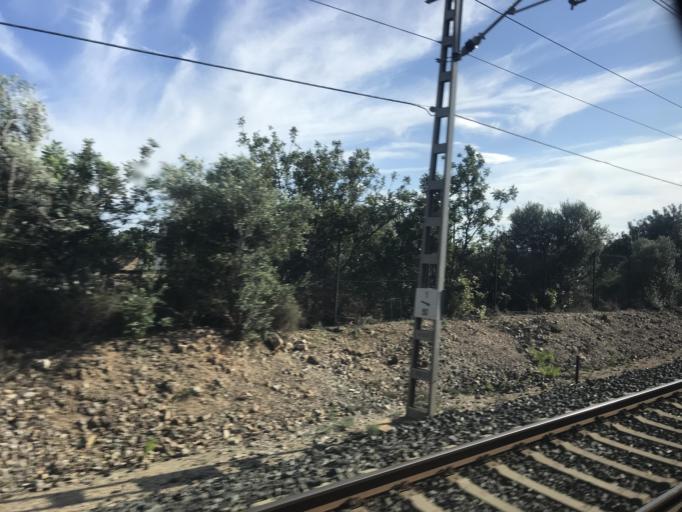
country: ES
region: Catalonia
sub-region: Provincia de Tarragona
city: l'Ametlla de Mar
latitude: 40.8806
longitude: 0.7952
